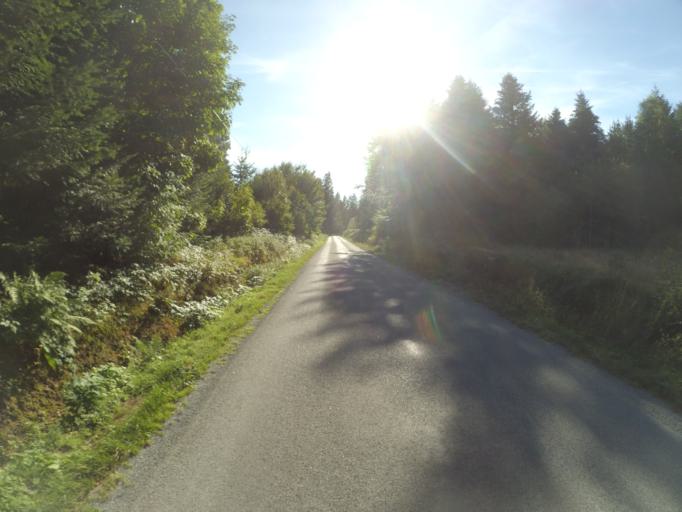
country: FR
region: Limousin
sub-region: Departement de la Creuse
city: Banize
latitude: 45.7839
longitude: 1.9857
